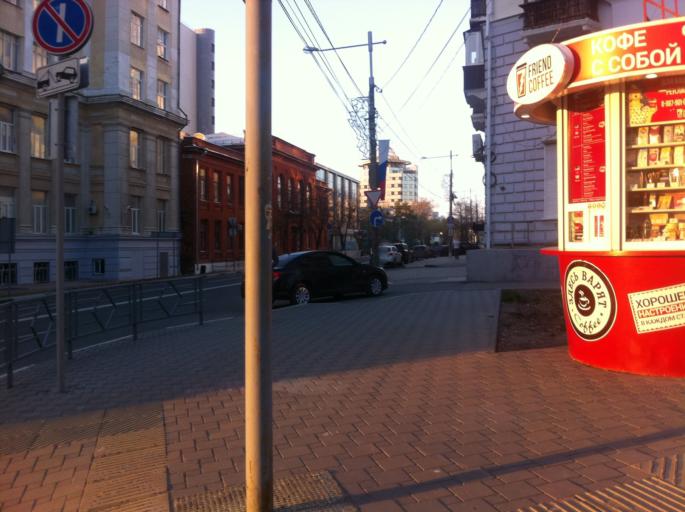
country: RU
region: Samara
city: Samara
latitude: 53.2000
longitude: 50.1058
